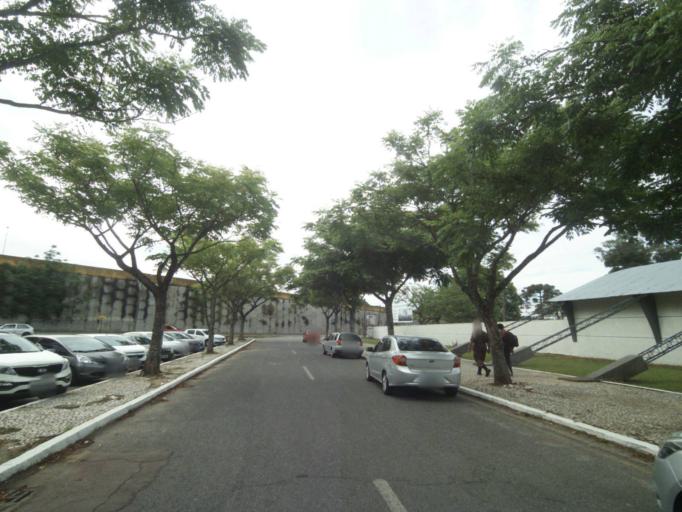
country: BR
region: Parana
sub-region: Pinhais
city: Pinhais
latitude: -25.4277
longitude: -49.2274
